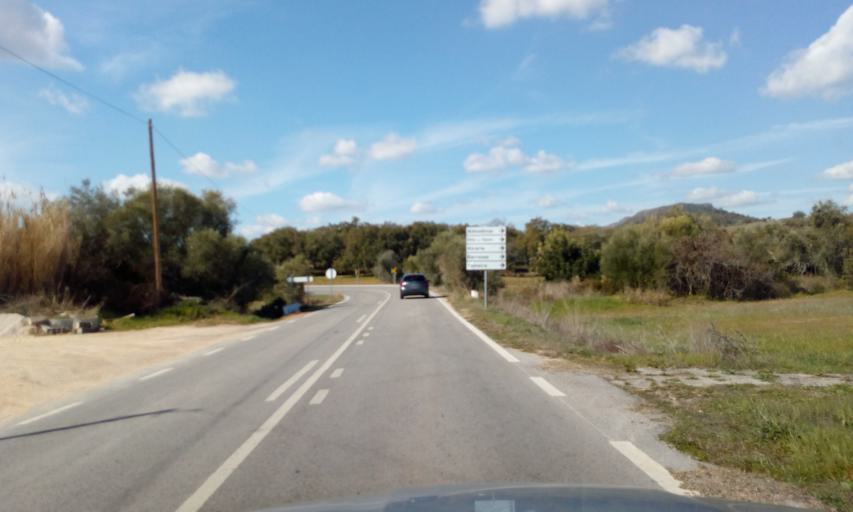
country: PT
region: Faro
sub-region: Loule
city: Loule
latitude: 37.2442
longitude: -8.0583
